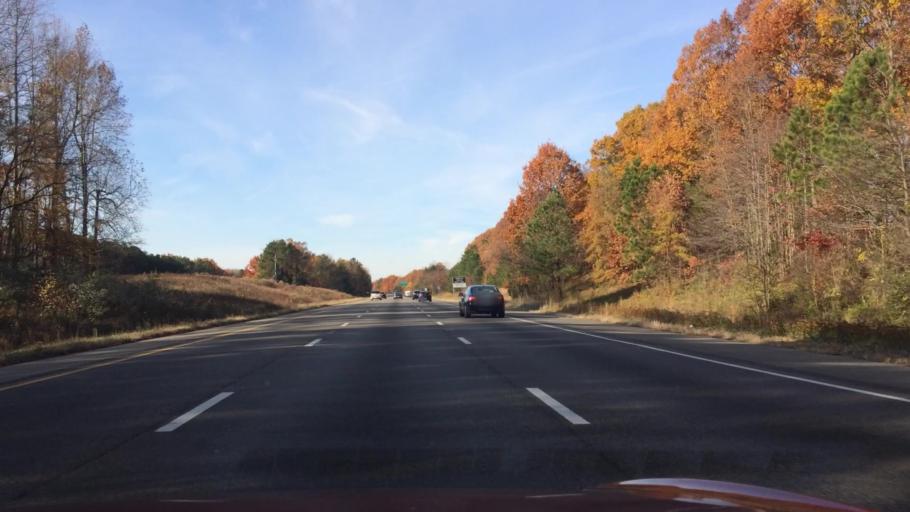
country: US
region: Virginia
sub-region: Henrico County
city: Glen Allen
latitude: 37.6794
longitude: -77.5498
